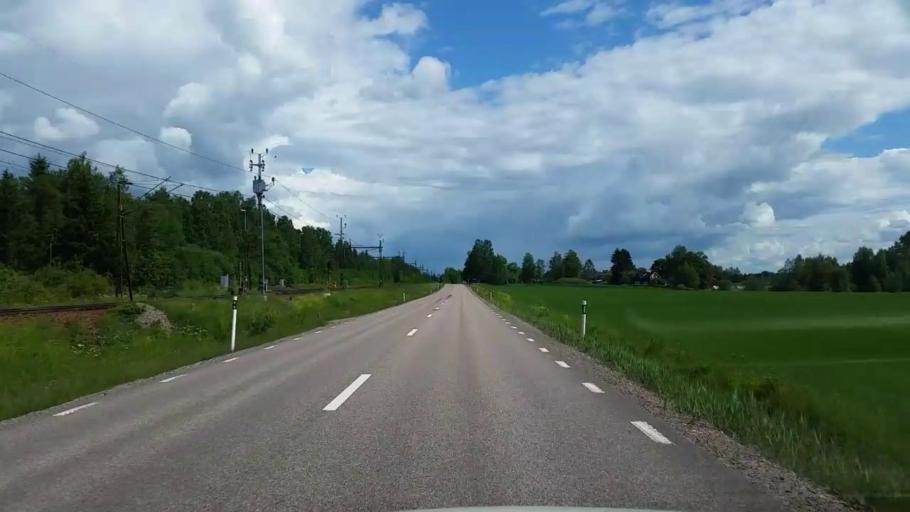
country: SE
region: Dalarna
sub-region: Avesta Kommun
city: Avesta
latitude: 60.1549
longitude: 16.2499
